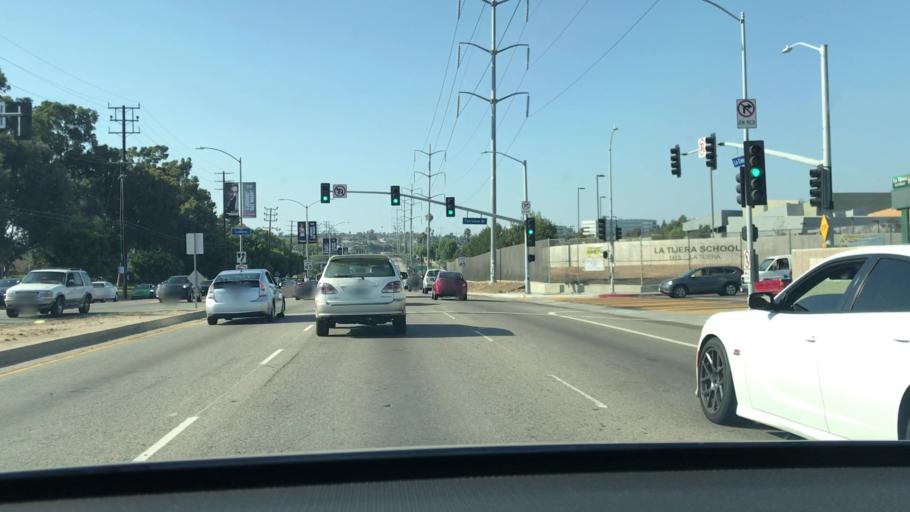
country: US
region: California
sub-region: Los Angeles County
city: Ladera Heights
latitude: 33.9795
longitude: -118.3703
